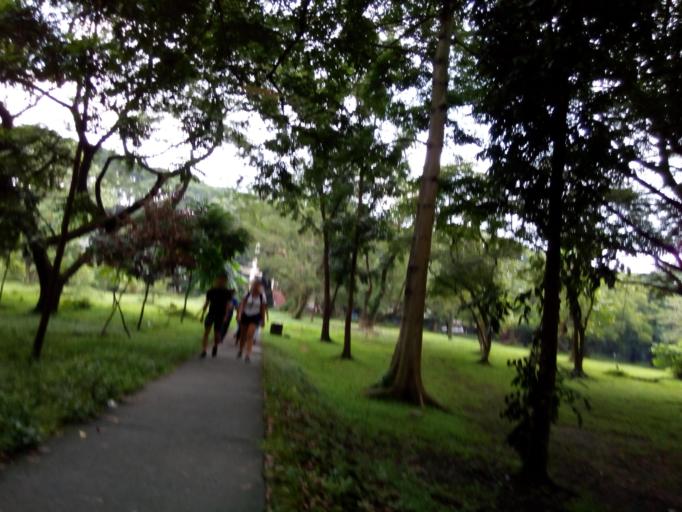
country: PH
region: Metro Manila
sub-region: Quezon City
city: Quezon City
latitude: 14.6550
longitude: 121.0697
